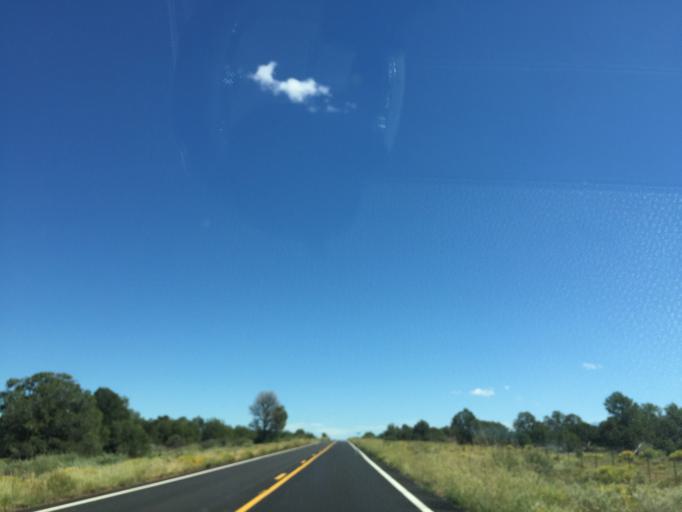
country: US
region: Arizona
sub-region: Coconino County
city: Parks
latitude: 35.6099
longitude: -112.0613
